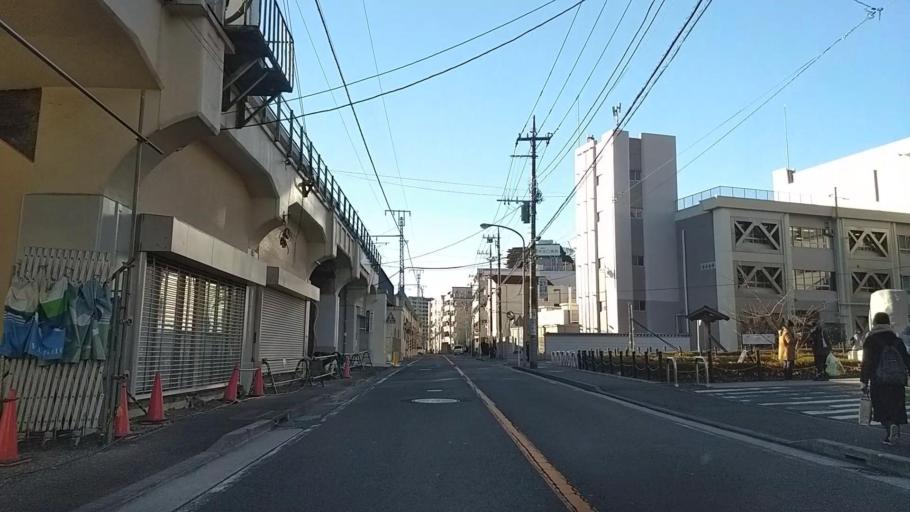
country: JP
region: Kanagawa
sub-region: Kawasaki-shi
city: Kawasaki
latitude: 35.5052
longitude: 139.6750
